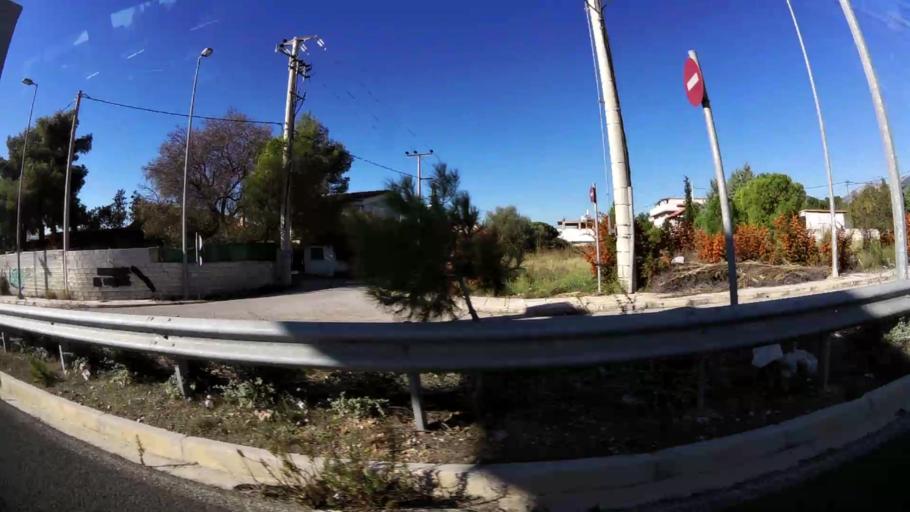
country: GR
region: Attica
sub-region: Nomarchia Anatolikis Attikis
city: Thrakomakedones
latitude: 38.1087
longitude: 23.7630
